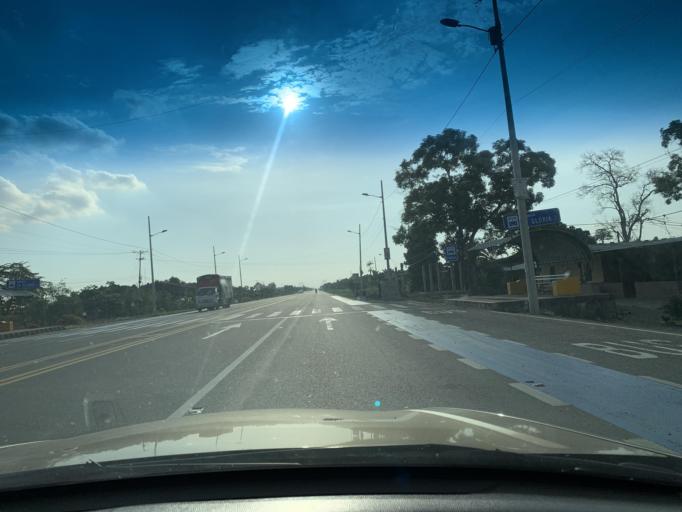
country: EC
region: Guayas
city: Naranjito
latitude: -2.2575
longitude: -79.5732
